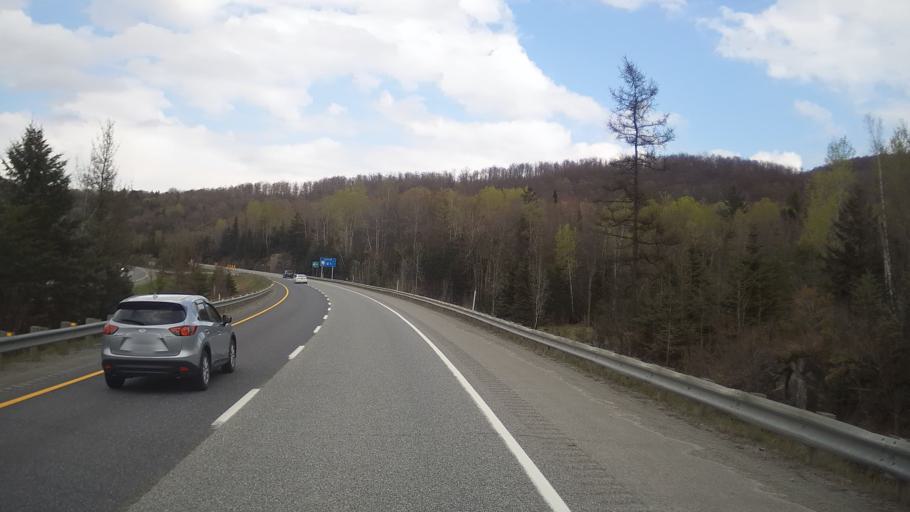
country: CA
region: Quebec
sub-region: Estrie
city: Magog
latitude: 45.2860
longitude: -72.2811
